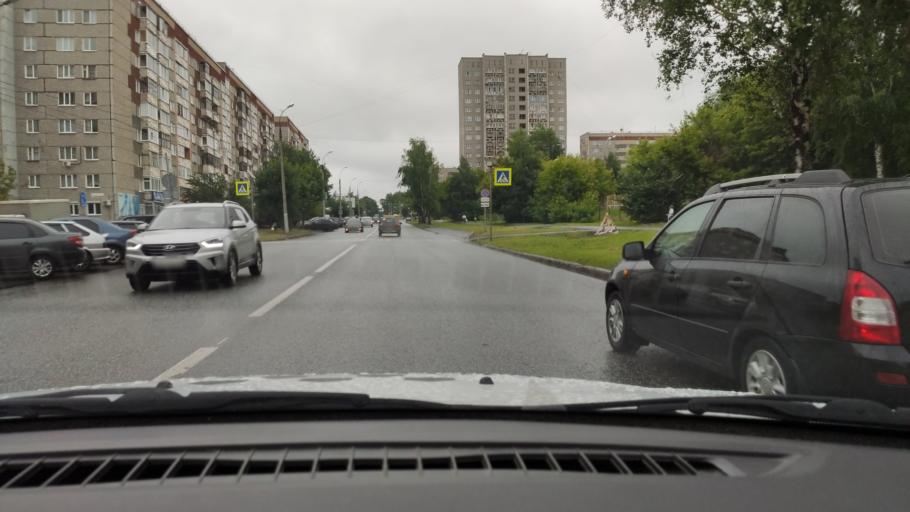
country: RU
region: Udmurtiya
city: Izhevsk
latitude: 56.8758
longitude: 53.2171
